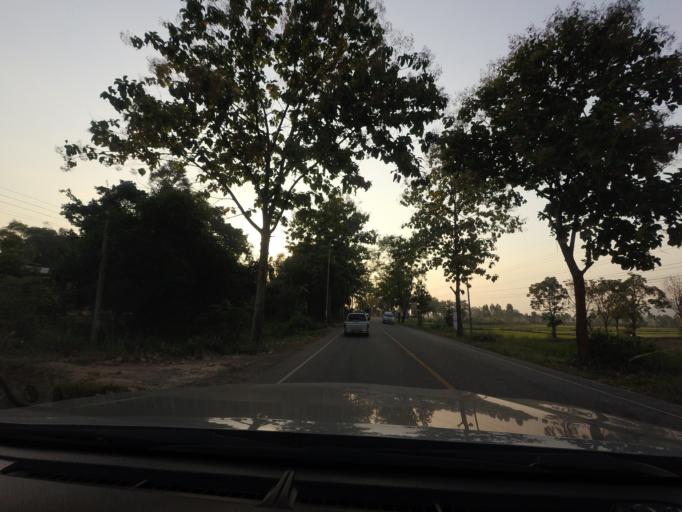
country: TH
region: Phitsanulok
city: Wang Thong
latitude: 16.7052
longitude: 100.4994
